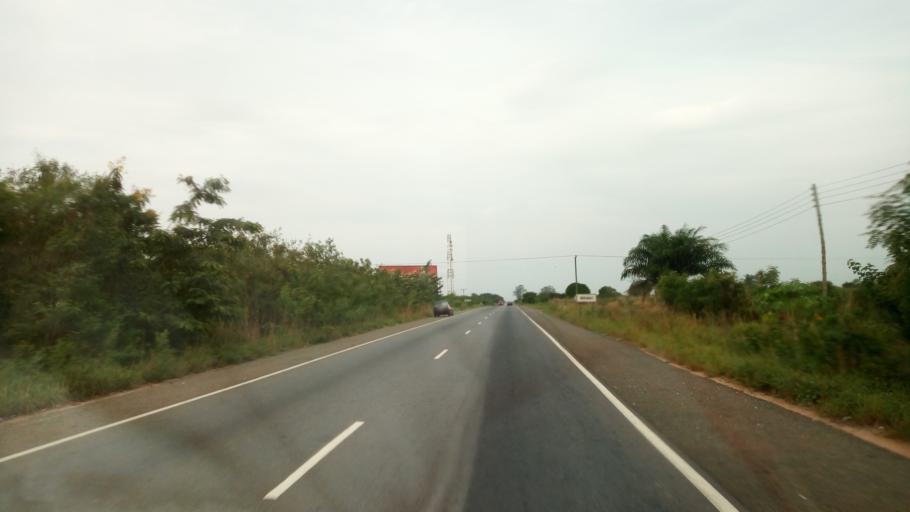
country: GH
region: Volta
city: Keta
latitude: 6.0644
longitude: 1.0081
